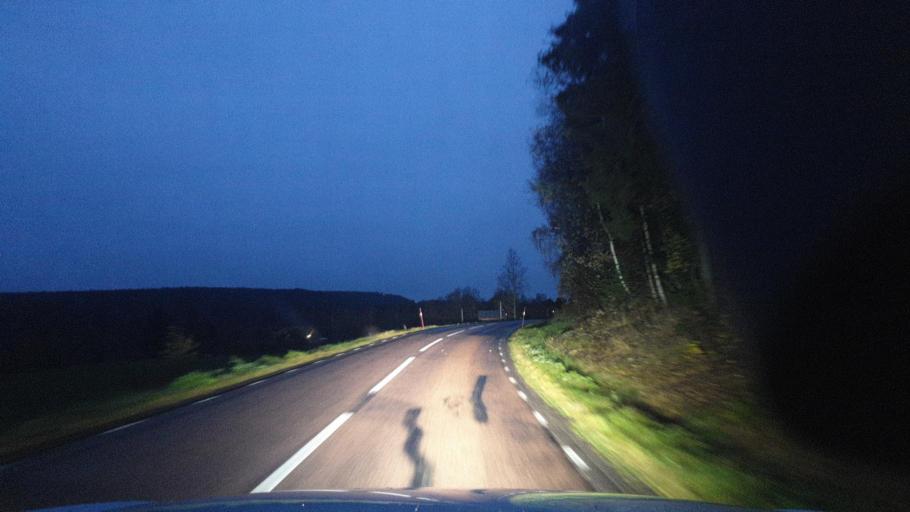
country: SE
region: Vaermland
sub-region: Eda Kommun
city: Amotfors
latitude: 59.7681
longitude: 12.2634
